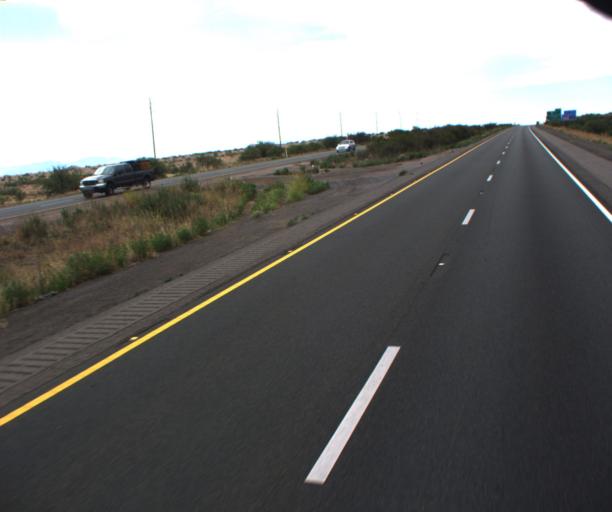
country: US
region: Arizona
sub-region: Yavapai County
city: Spring Valley
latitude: 34.3510
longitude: -112.1175
